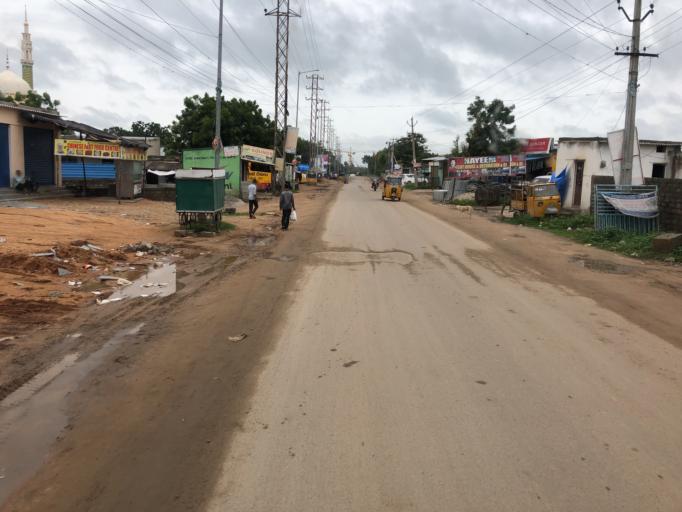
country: IN
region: Telangana
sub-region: Medak
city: Serilingampalle
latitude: 17.4398
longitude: 78.3030
